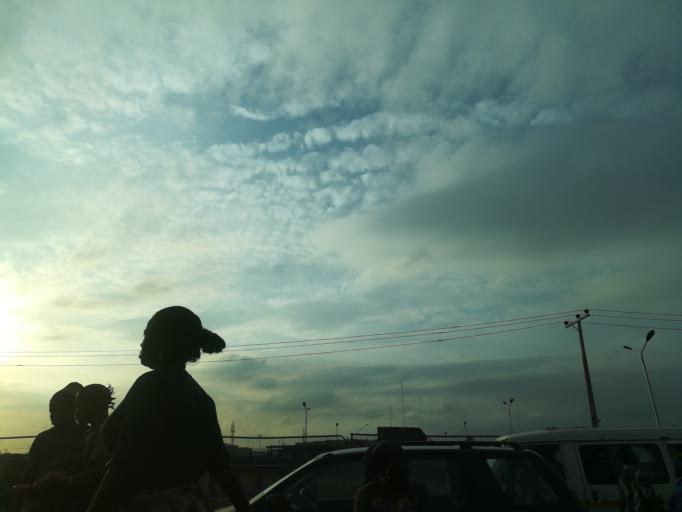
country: NG
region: Lagos
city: Ojota
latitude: 6.5974
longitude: 3.3857
